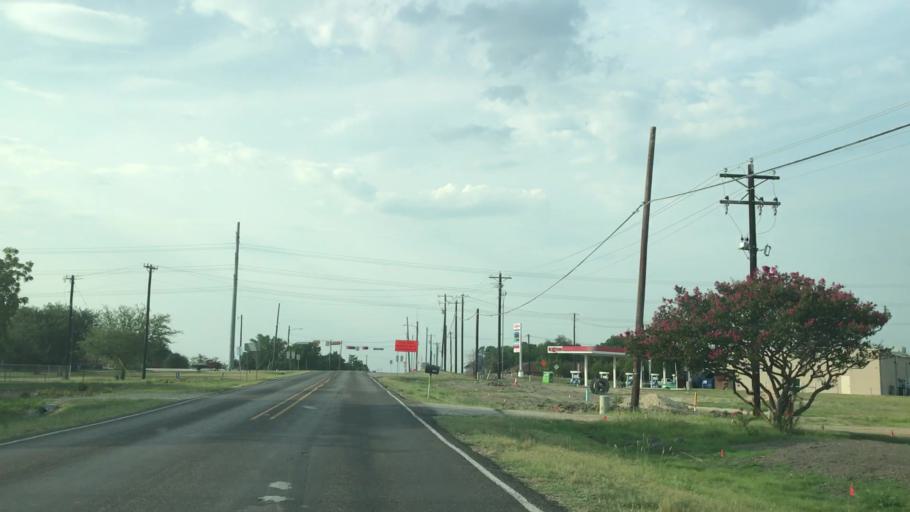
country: US
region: Texas
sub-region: Rockwall County
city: Fate
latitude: 32.9347
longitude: -96.4180
